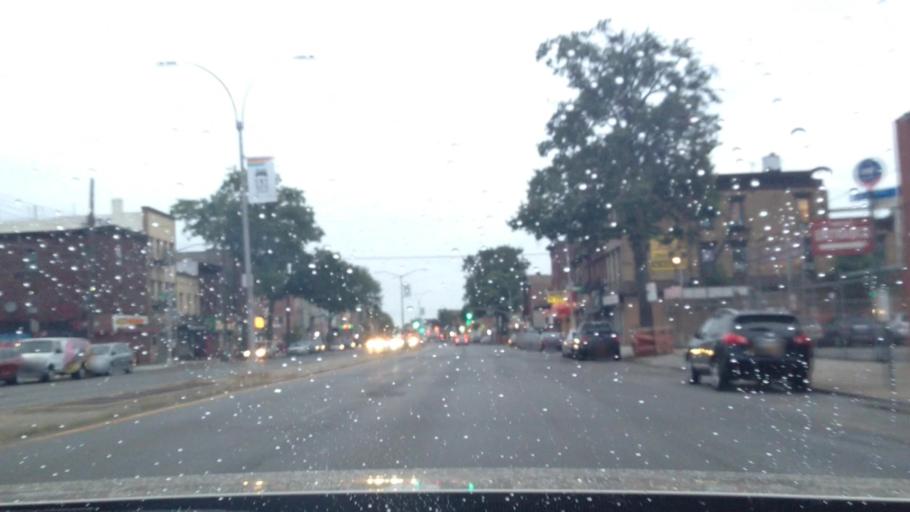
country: US
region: New York
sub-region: Kings County
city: East New York
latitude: 40.6759
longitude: -73.8947
